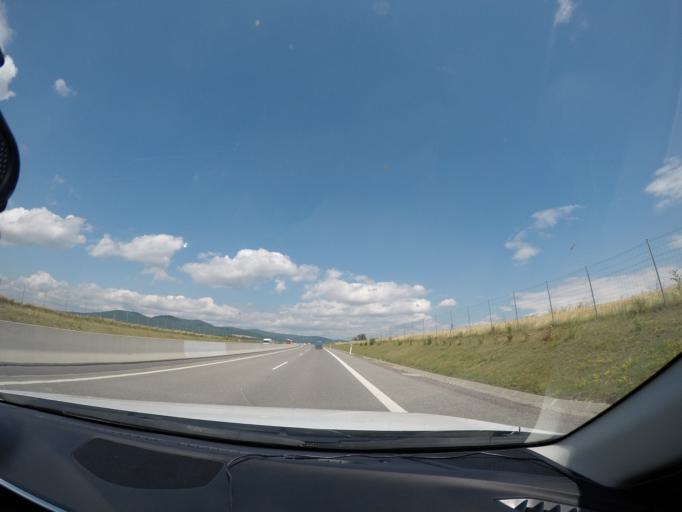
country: SK
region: Nitriansky
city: Zlate Moravce
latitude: 48.3435
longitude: 18.4269
